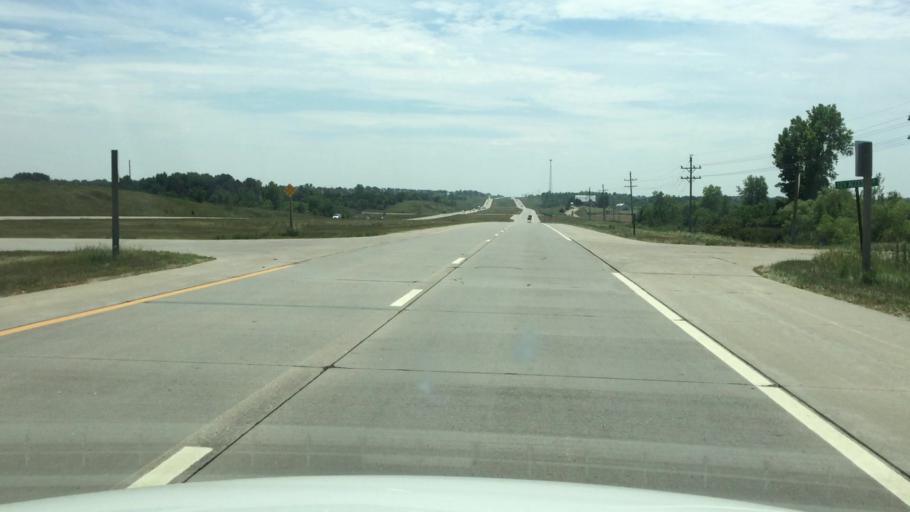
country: US
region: Kansas
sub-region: Jackson County
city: Holton
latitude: 39.2657
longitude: -95.7201
